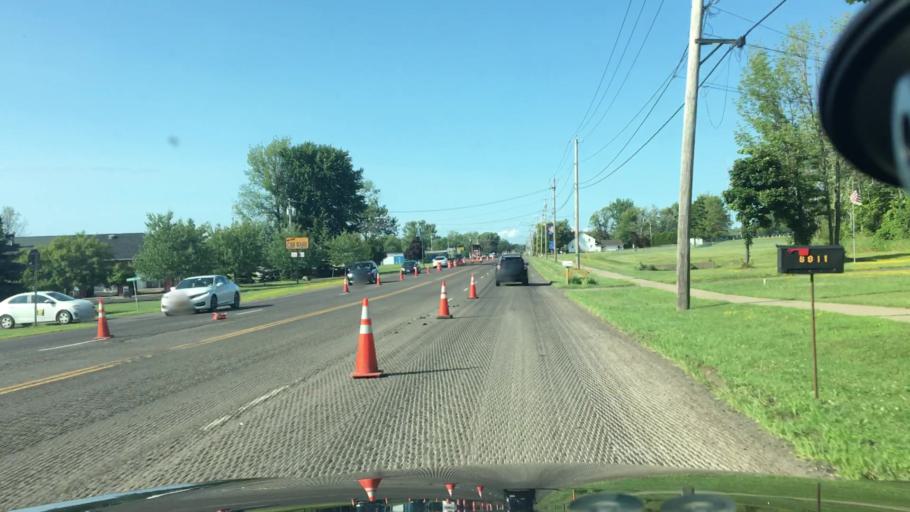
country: US
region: New York
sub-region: Erie County
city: Angola on the Lake
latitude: 42.6426
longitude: -79.0454
